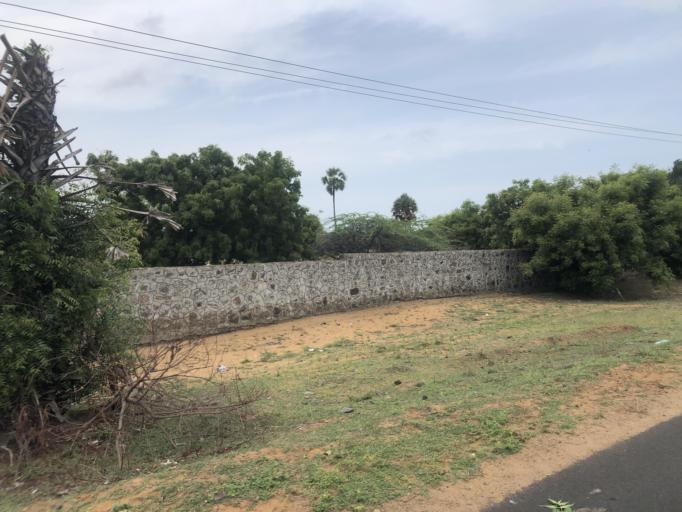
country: IN
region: Tamil Nadu
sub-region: Kancheepuram
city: Mamallapuram
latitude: 12.6016
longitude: 80.1877
